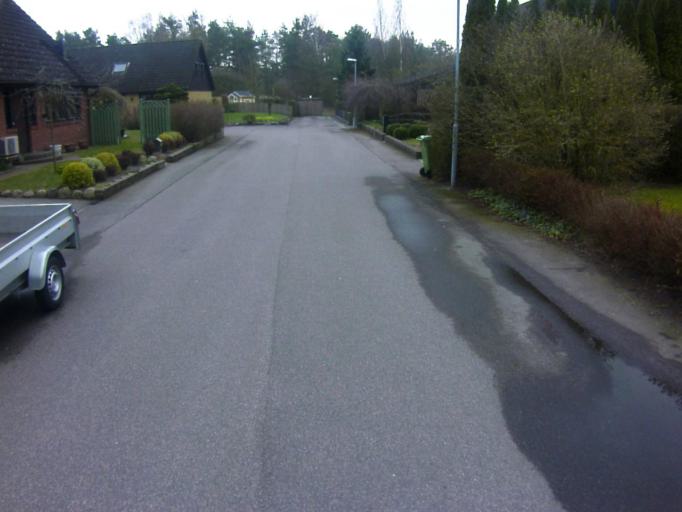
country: SE
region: Skane
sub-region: Kavlinge Kommun
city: Kaevlinge
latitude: 55.7752
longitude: 13.0734
